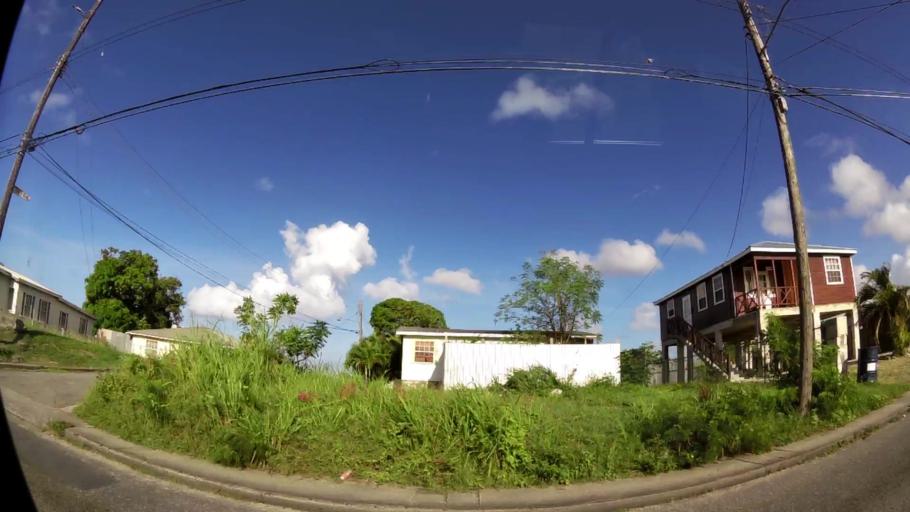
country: BB
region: Saint Michael
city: Bridgetown
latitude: 13.1073
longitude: -59.5963
